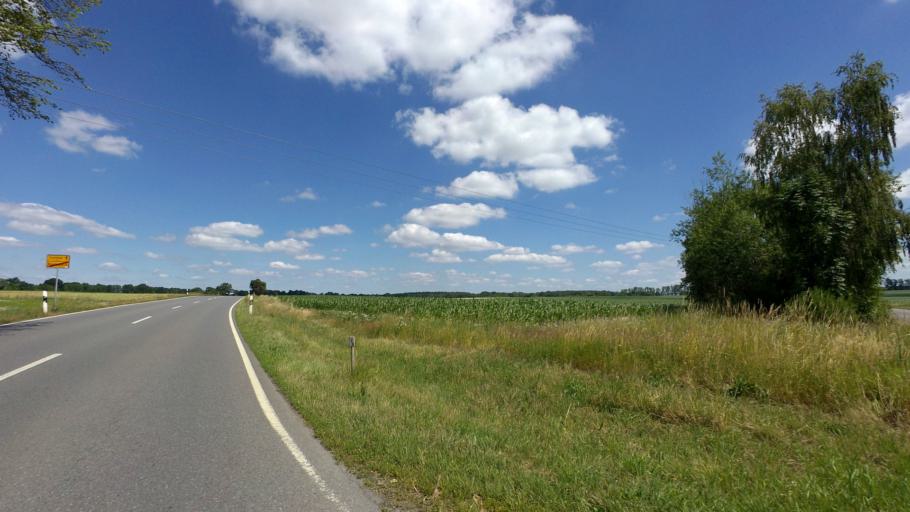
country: DE
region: Brandenburg
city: Luckau
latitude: 51.8063
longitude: 13.6781
